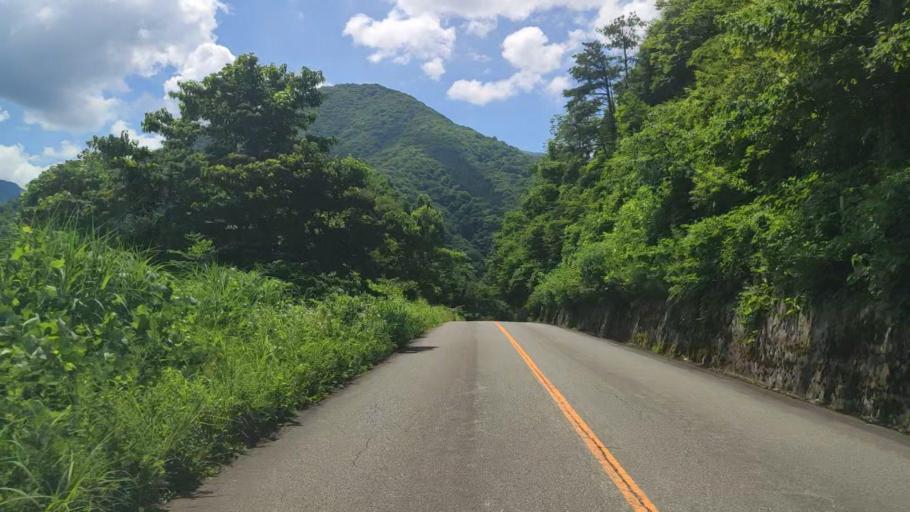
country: JP
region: Fukui
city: Ono
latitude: 35.9054
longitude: 136.5322
